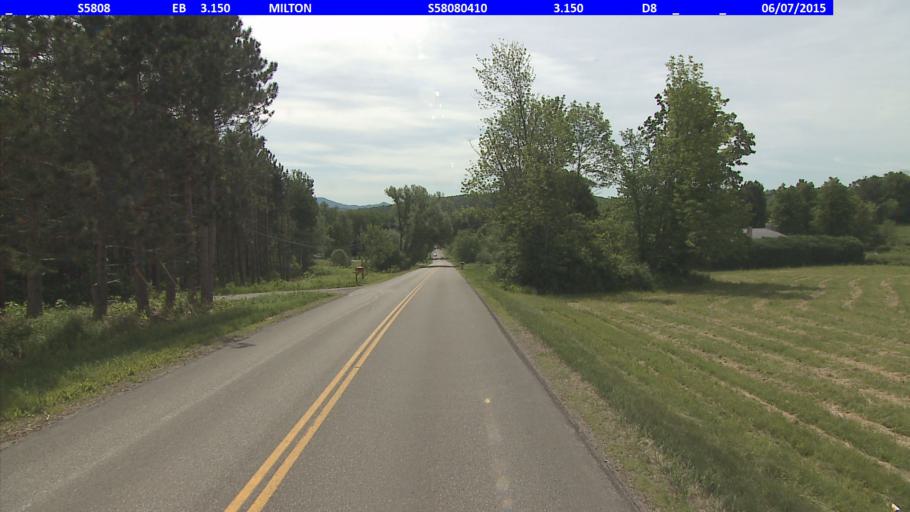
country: US
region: Vermont
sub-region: Chittenden County
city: Milton
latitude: 44.6410
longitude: -73.0571
